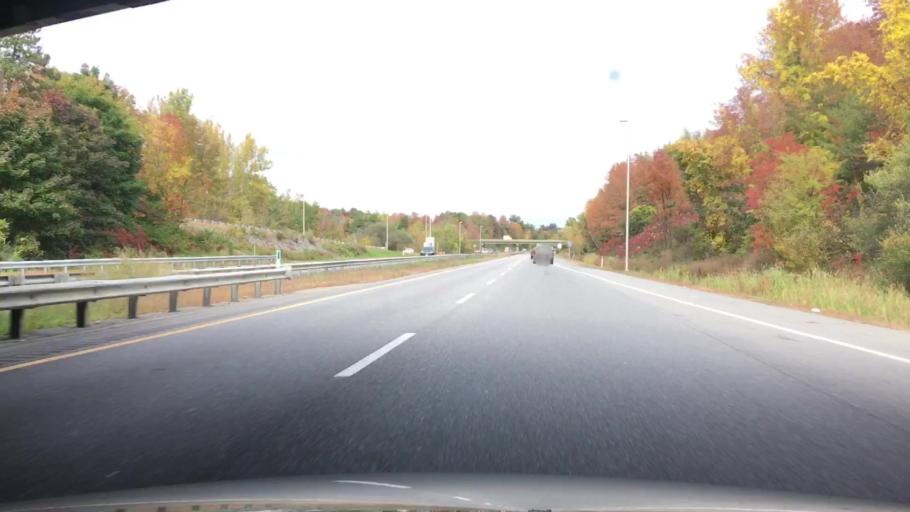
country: US
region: Maine
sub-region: Kennebec County
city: Augusta
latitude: 44.3166
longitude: -69.8116
